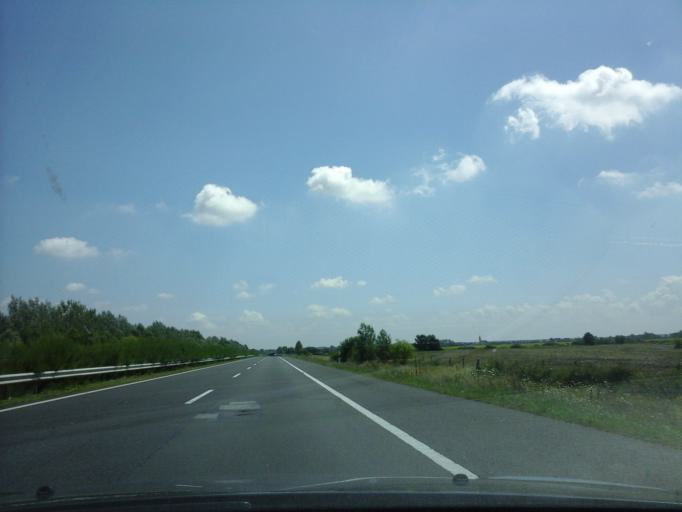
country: HU
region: Borsod-Abauj-Zemplen
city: Hejobaba
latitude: 47.8696
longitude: 20.9724
